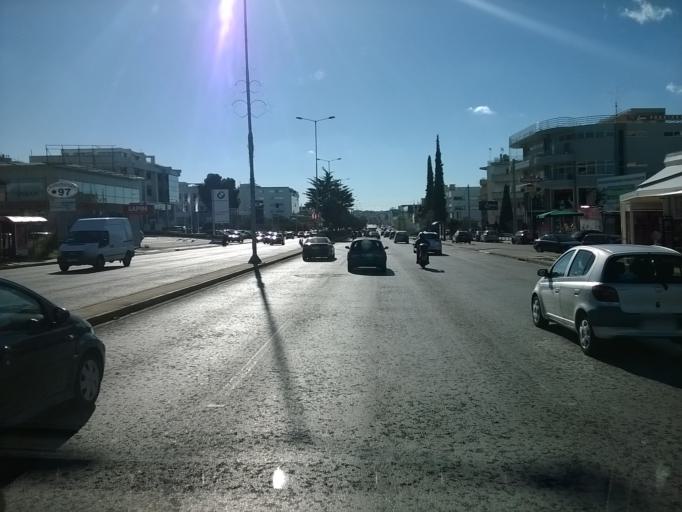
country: GR
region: Attica
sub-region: Nomarchia Athinas
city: Glyfada
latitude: 37.8692
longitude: 23.7595
